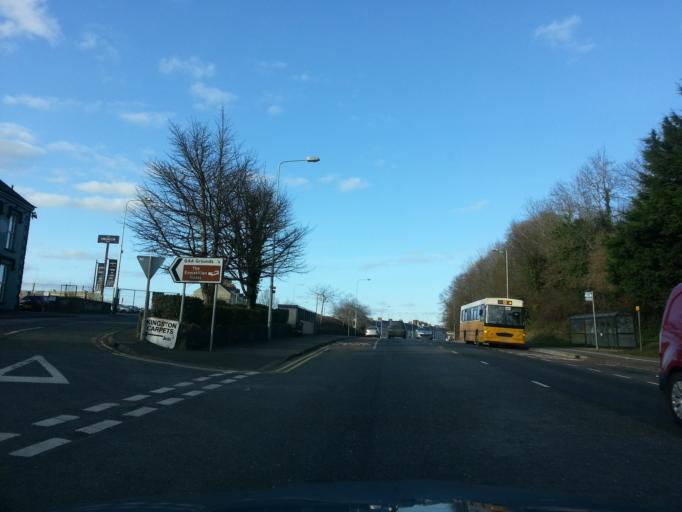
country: GB
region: Northern Ireland
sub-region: Fermanagh District
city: Enniskillen
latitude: 54.3458
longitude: -7.6300
